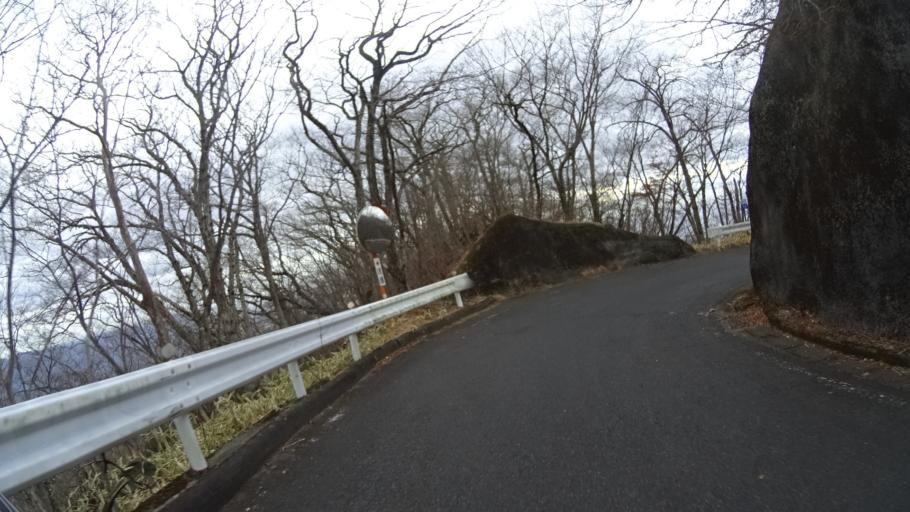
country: JP
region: Gunma
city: Omamacho-omama
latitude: 36.5175
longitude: 139.1832
